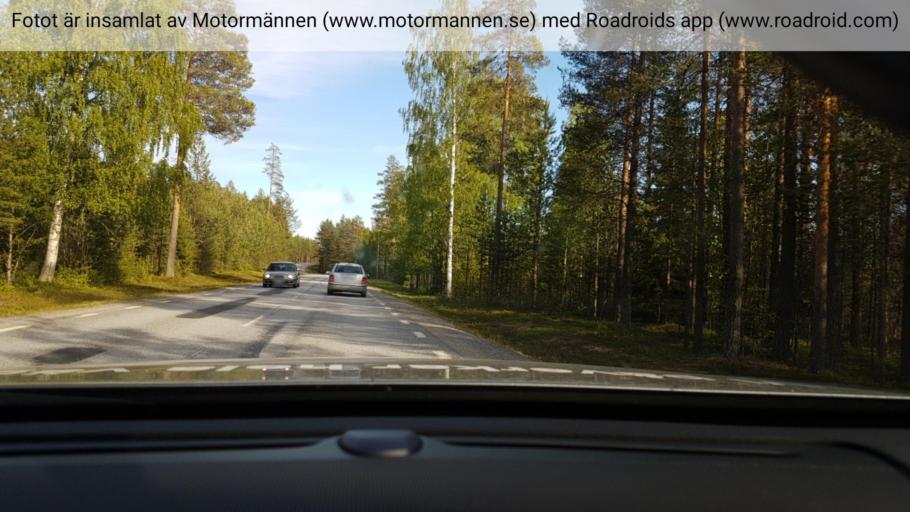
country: SE
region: Vaesterbotten
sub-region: Vindelns Kommun
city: Vindeln
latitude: 64.2484
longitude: 19.6450
